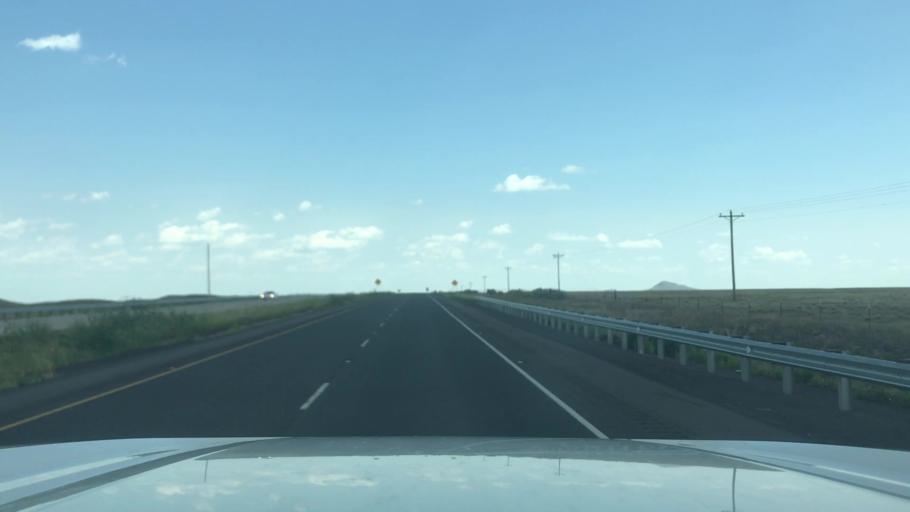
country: US
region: New Mexico
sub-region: Union County
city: Clayton
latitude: 36.6250
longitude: -103.7031
